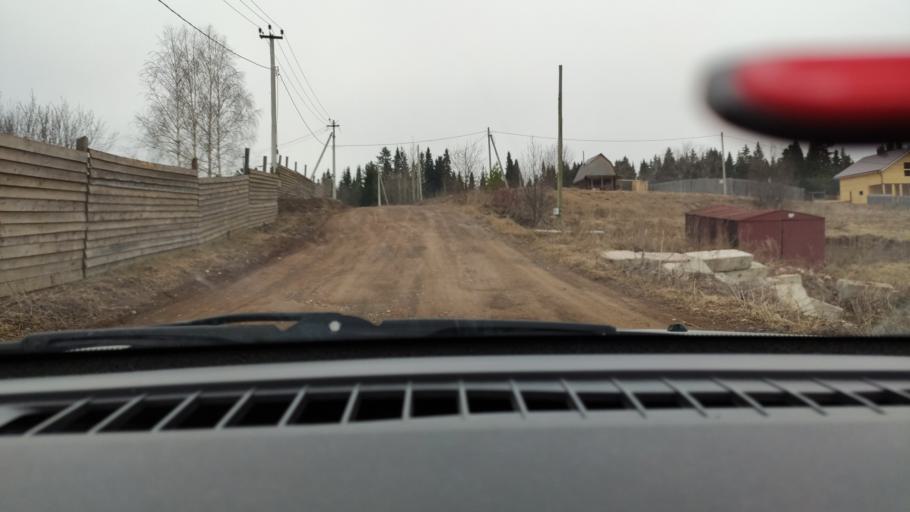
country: RU
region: Perm
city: Kultayevo
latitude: 57.8975
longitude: 56.0132
